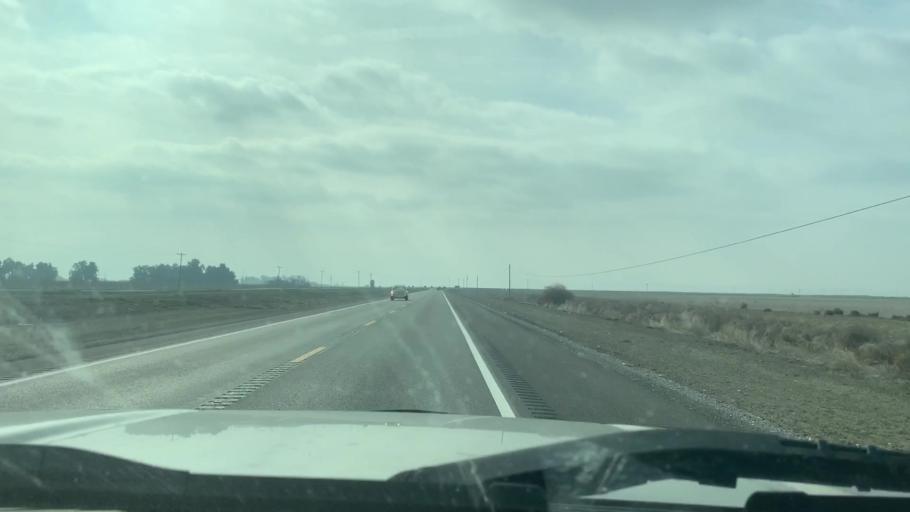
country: US
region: California
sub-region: Kings County
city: Stratford
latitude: 36.1418
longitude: -119.8742
